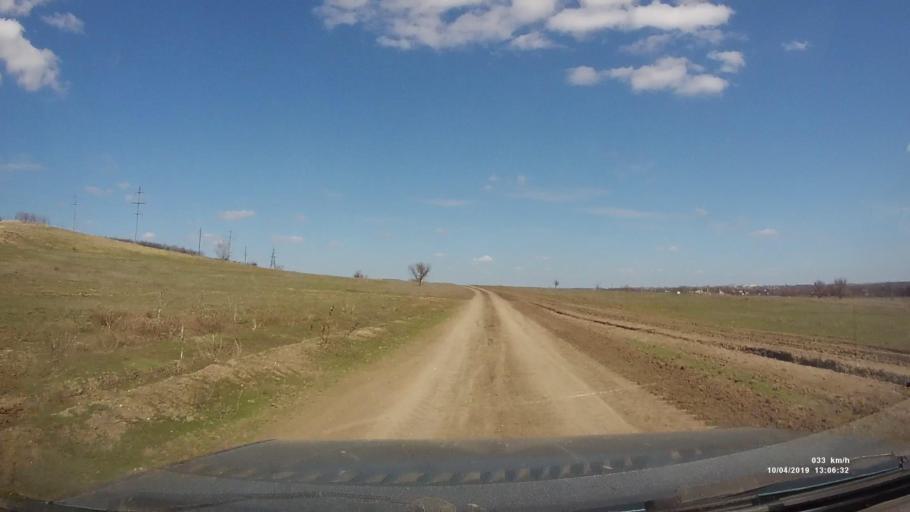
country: RU
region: Rostov
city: Masalovka
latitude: 48.3923
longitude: 40.2369
